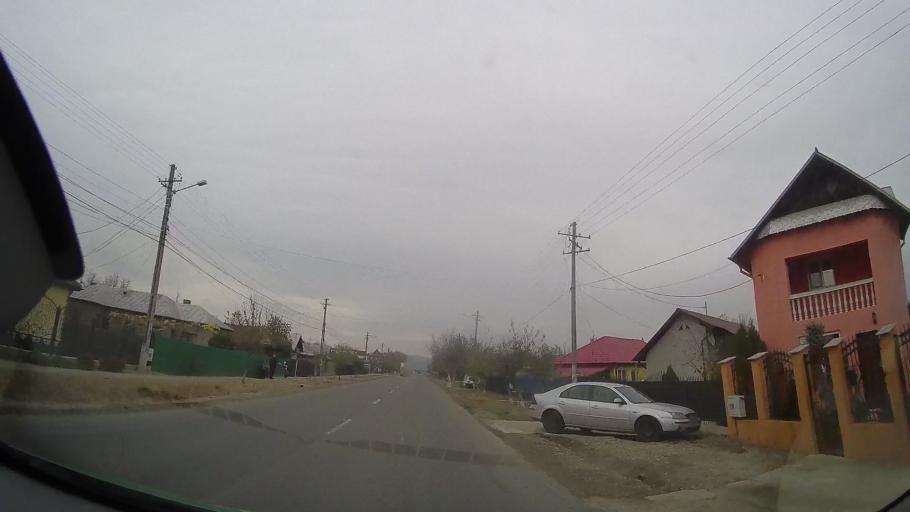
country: RO
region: Prahova
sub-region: Comuna Albesti-Paleologu
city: Albesti-Paleologu
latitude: 44.9604
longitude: 26.2327
